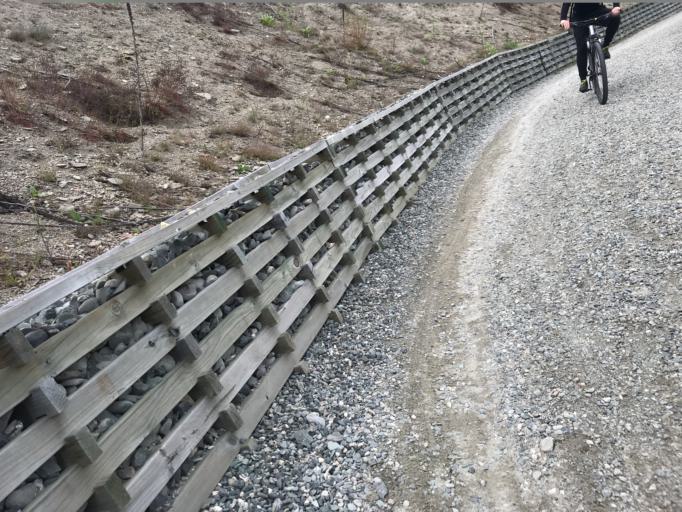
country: NZ
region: Otago
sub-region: Queenstown-Lakes District
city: Arrowtown
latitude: -45.0029
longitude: 168.8790
